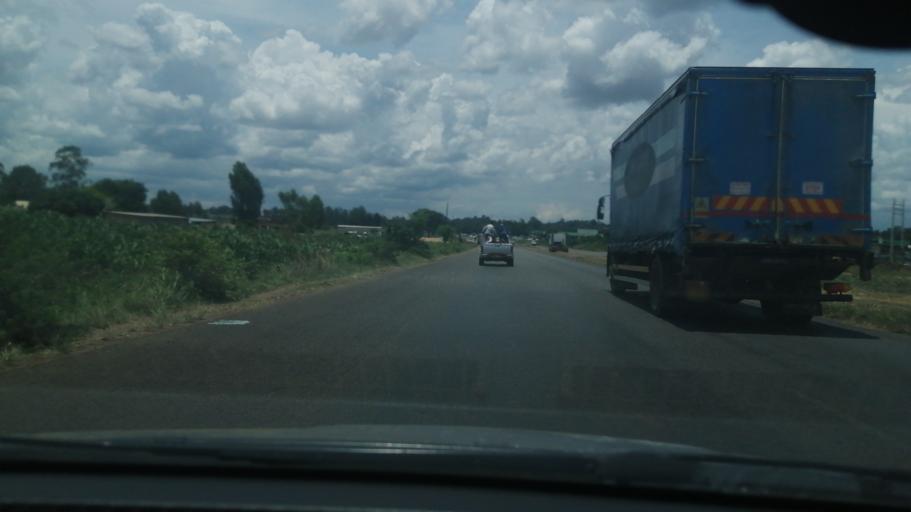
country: ZW
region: Harare
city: Harare
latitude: -17.8227
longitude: 30.9675
